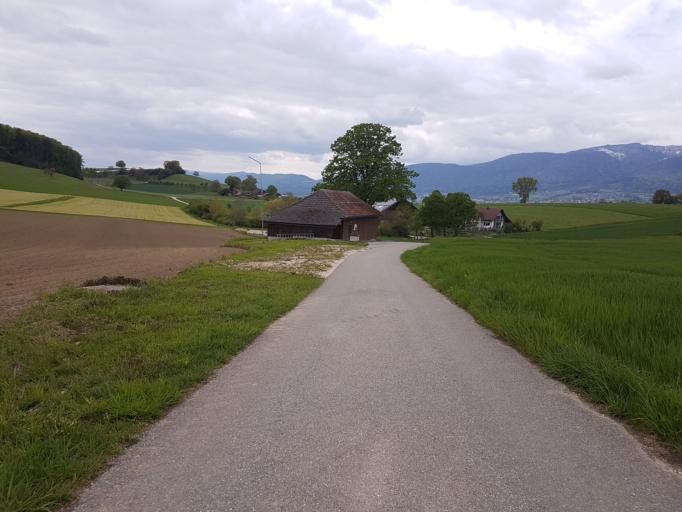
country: CH
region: Bern
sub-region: Seeland District
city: Leuzigen
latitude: 47.1808
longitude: 7.4875
